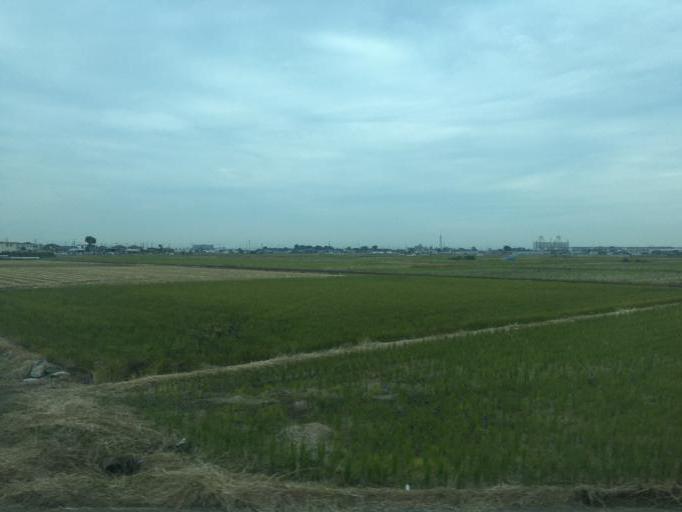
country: JP
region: Saitama
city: Kamifukuoka
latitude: 35.9038
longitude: 139.5293
